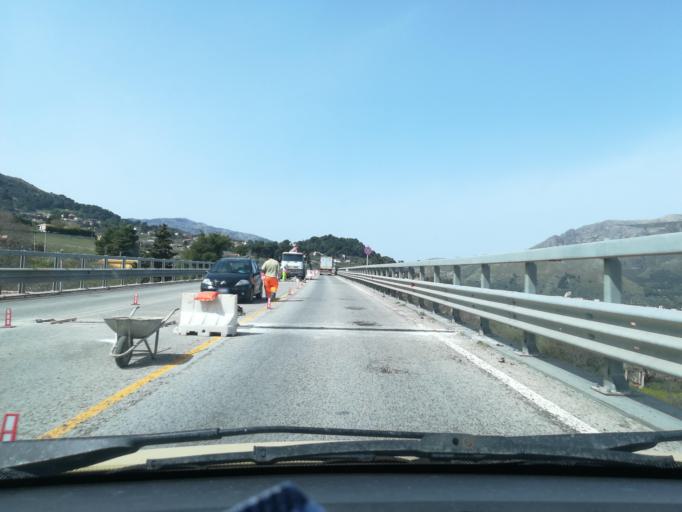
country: IT
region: Sicily
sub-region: Palermo
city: Giacalone
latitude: 38.0341
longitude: 13.2515
